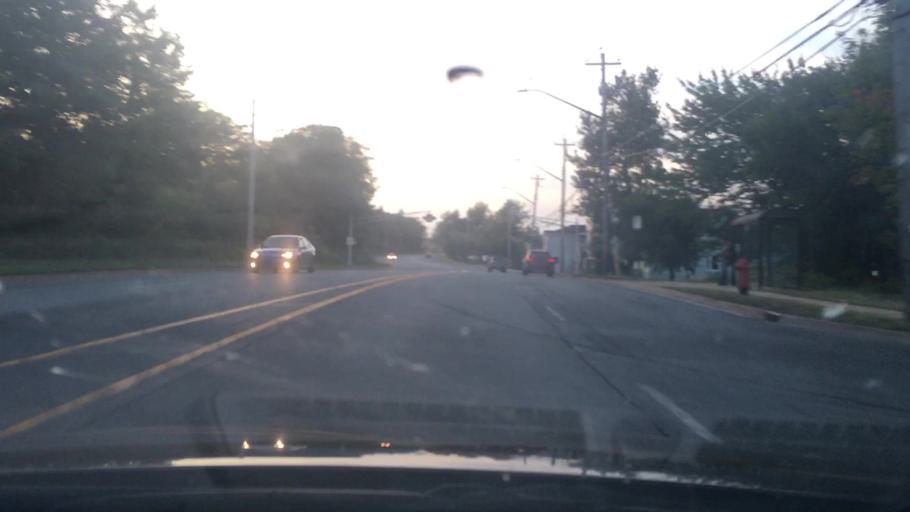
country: CA
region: Nova Scotia
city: Halifax
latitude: 44.6356
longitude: -63.5266
